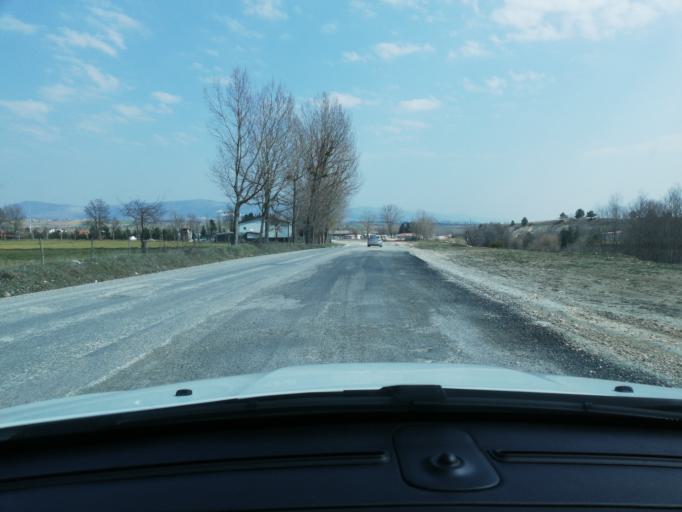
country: TR
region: Kastamonu
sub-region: Cide
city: Kastamonu
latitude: 41.4454
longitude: 33.7611
